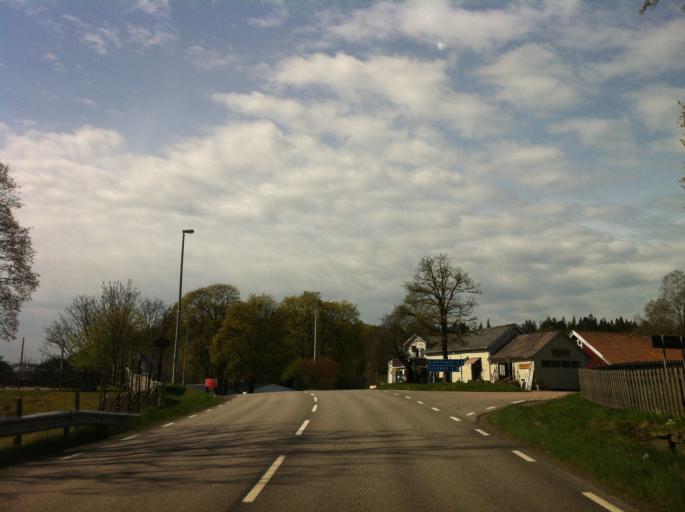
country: SE
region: Vaestra Goetaland
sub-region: Marks Kommun
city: Horred
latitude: 57.1646
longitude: 12.7475
